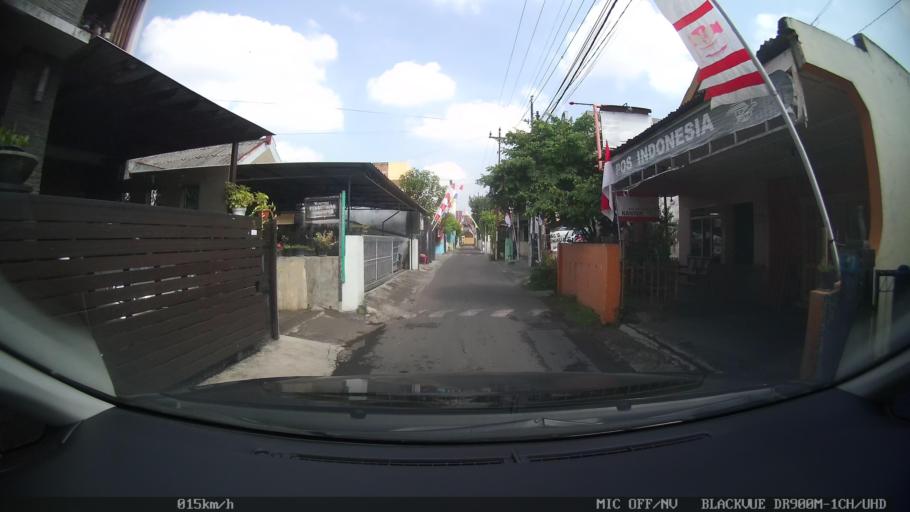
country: ID
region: Daerah Istimewa Yogyakarta
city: Yogyakarta
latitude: -7.8120
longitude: 110.3781
